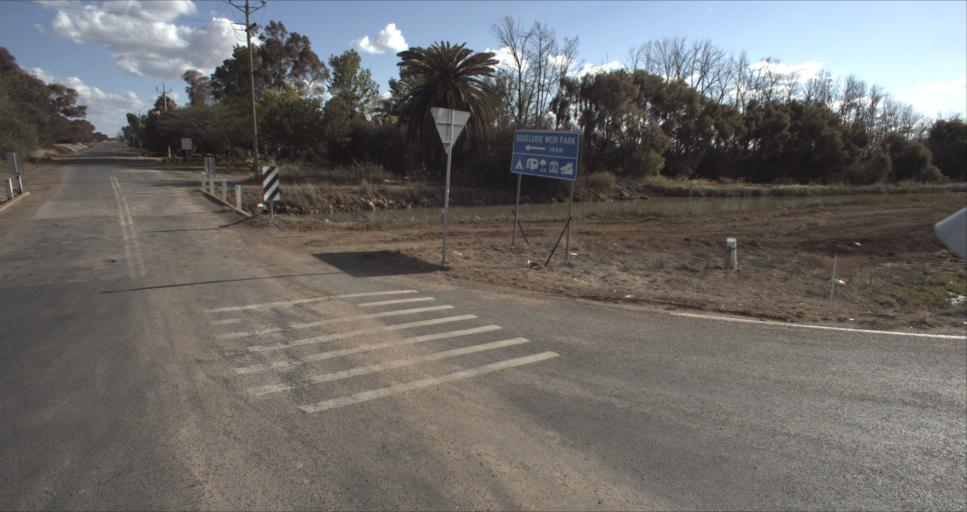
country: AU
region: New South Wales
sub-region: Leeton
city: Leeton
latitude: -34.5200
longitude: 146.2835
